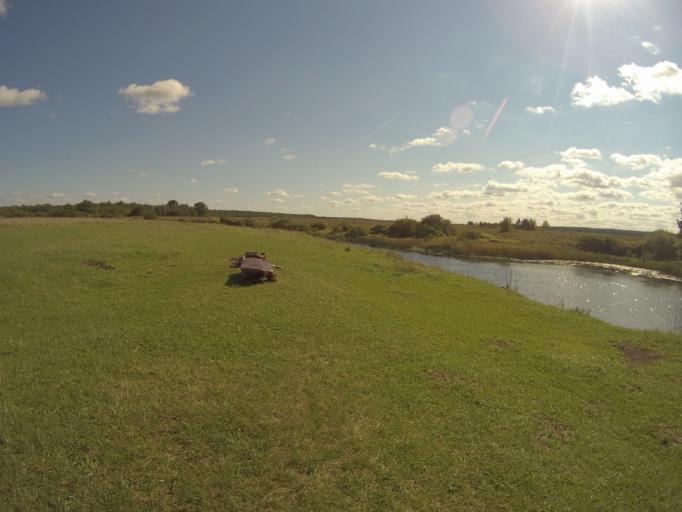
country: RU
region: Vladimir
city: Orgtrud
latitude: 56.2975
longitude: 40.6171
